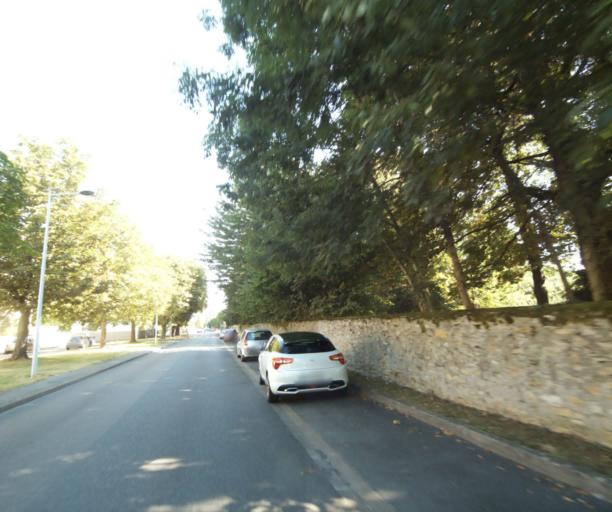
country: FR
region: Ile-de-France
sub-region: Departement de Seine-et-Marne
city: Moissy-Cramayel
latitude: 48.6241
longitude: 2.5846
